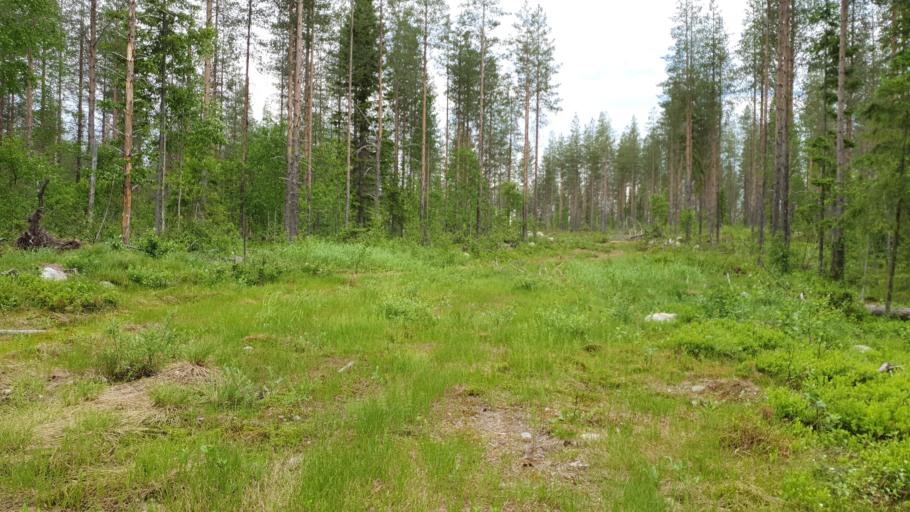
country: FI
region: Kainuu
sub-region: Kehys-Kainuu
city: Kuhmo
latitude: 64.4454
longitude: 29.6837
